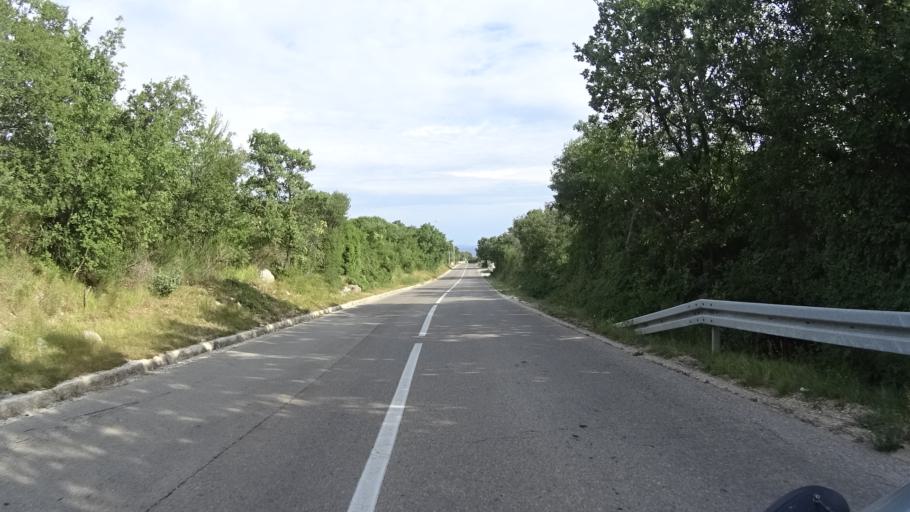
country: HR
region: Istarska
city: Rasa
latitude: 44.9880
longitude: 14.1143
